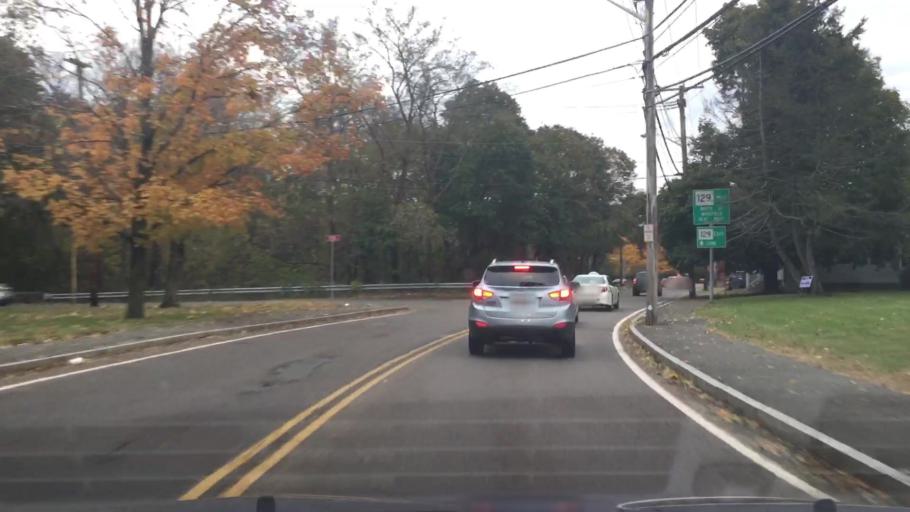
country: US
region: Massachusetts
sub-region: Essex County
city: Saugus
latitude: 42.4998
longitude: -71.0205
